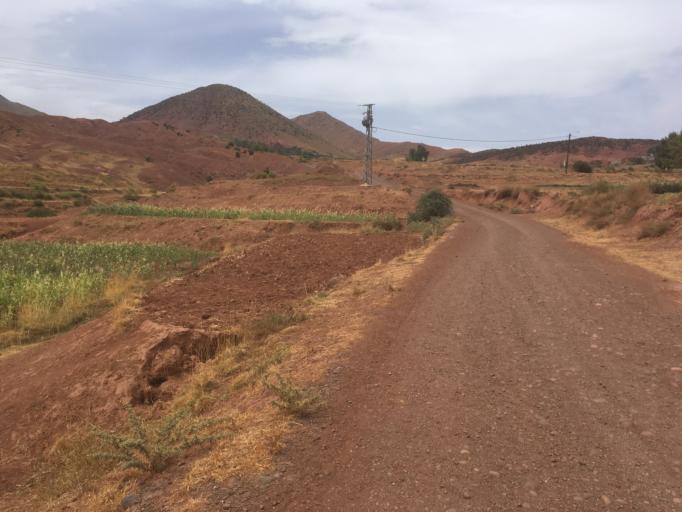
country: MA
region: Marrakech-Tensift-Al Haouz
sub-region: Al-Haouz
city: Tidili Mesfioua
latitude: 31.3816
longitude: -7.5884
